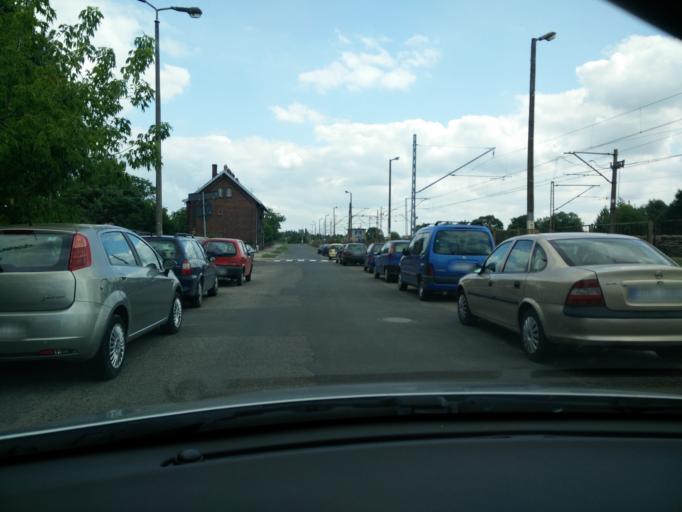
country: PL
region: Greater Poland Voivodeship
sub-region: Powiat sredzki
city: Sroda Wielkopolska
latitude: 52.2178
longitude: 17.2758
